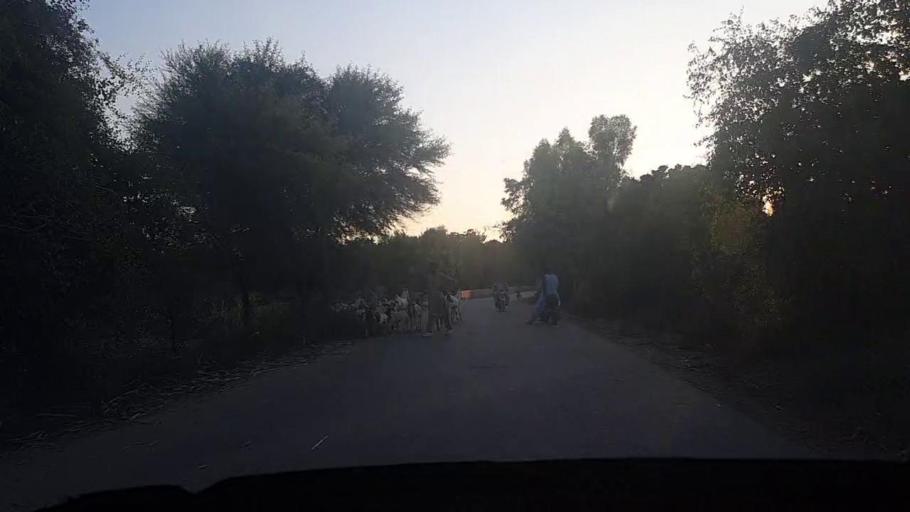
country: PK
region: Sindh
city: Sobhadero
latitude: 27.3375
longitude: 68.3780
